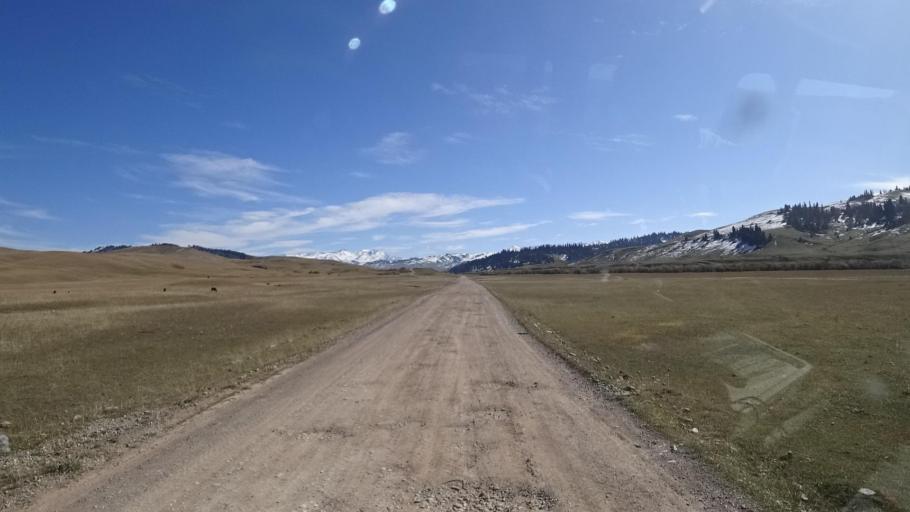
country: KZ
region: Almaty Oblysy
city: Kegen
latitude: 42.7416
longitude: 79.0021
